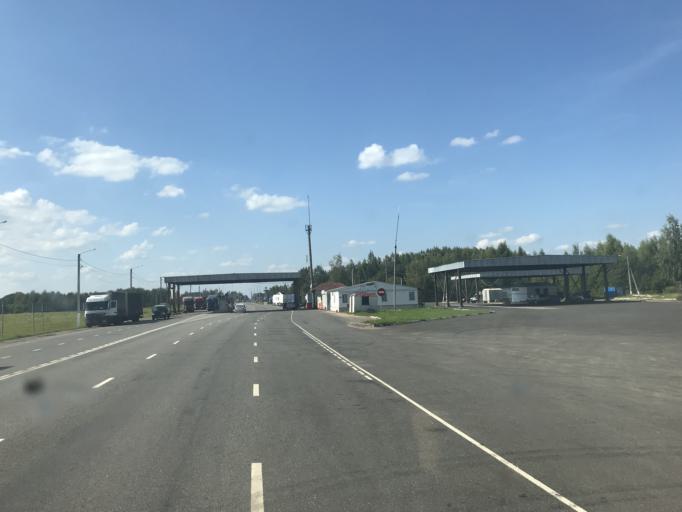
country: RU
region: Smolensk
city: Rudnya
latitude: 54.9876
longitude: 30.9569
